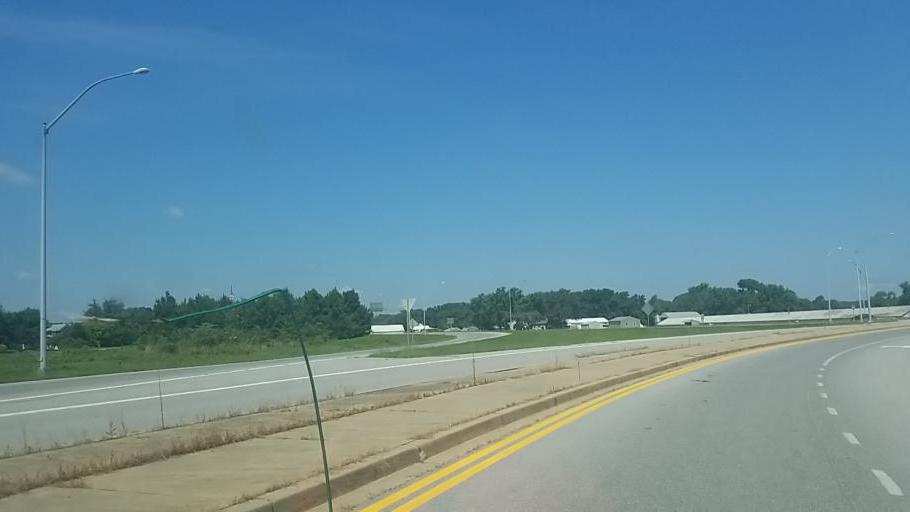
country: US
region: Maryland
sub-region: Caroline County
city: Denton
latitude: 38.8956
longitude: -75.8529
